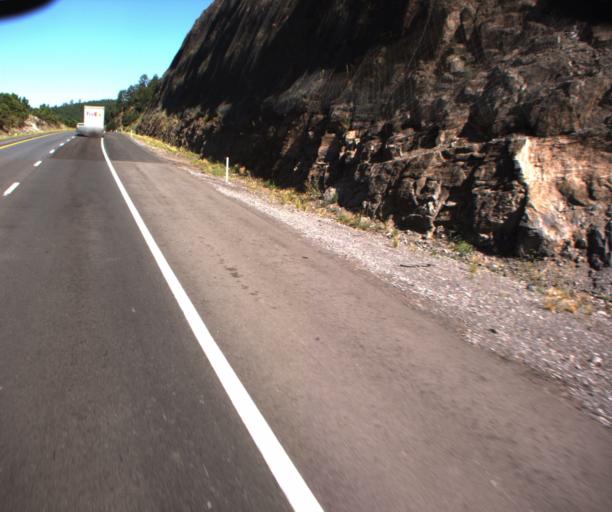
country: US
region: Arizona
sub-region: Coconino County
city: Parks
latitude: 35.2491
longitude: -111.8928
